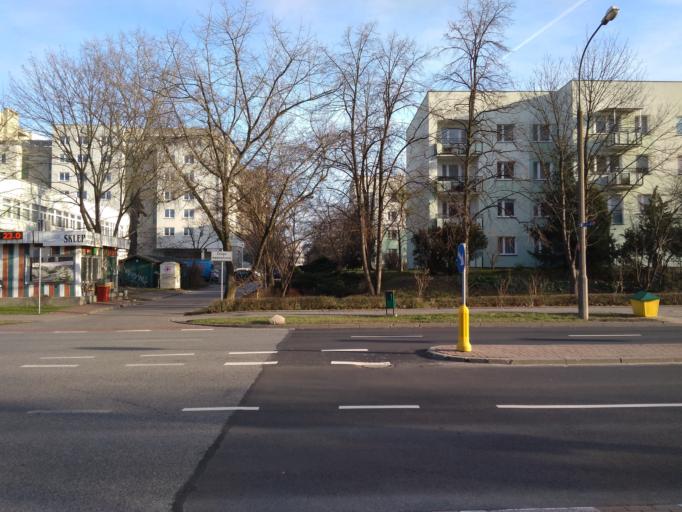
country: PL
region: Masovian Voivodeship
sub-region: Warszawa
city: Ursynow
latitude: 52.1608
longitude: 21.0362
